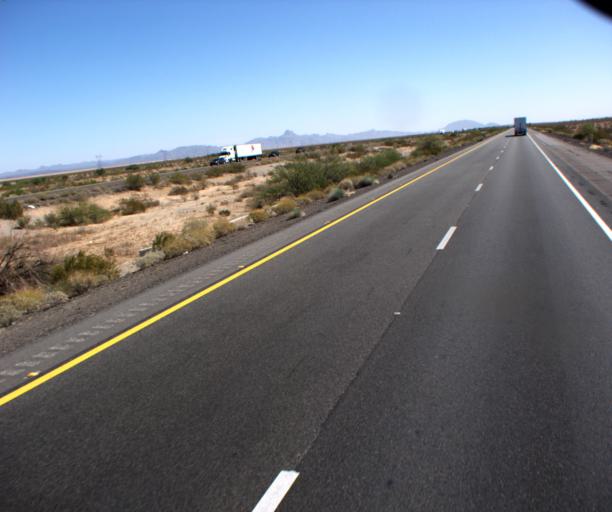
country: US
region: Arizona
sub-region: La Paz County
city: Salome
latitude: 33.5735
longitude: -113.3847
